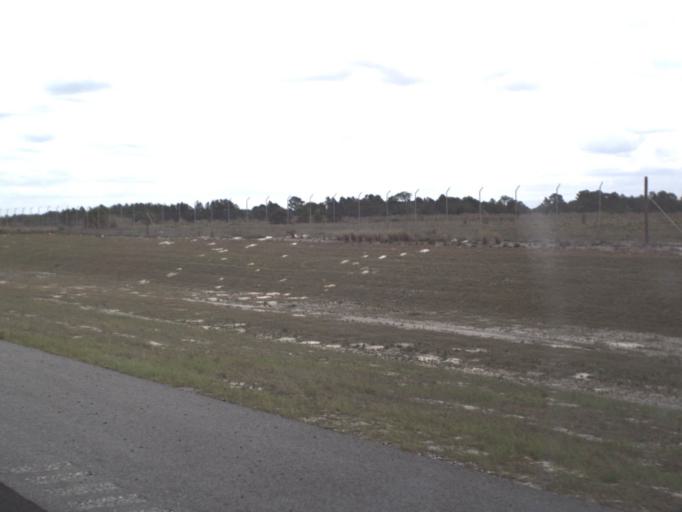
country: US
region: Florida
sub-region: Lake County
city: Mount Plymouth
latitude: 28.8039
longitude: -81.5136
